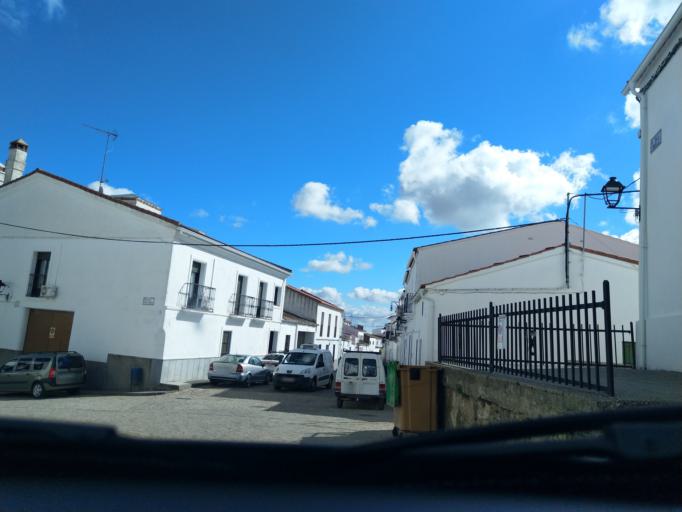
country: ES
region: Extremadura
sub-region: Provincia de Badajoz
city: Reina
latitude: 38.1508
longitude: -5.8973
